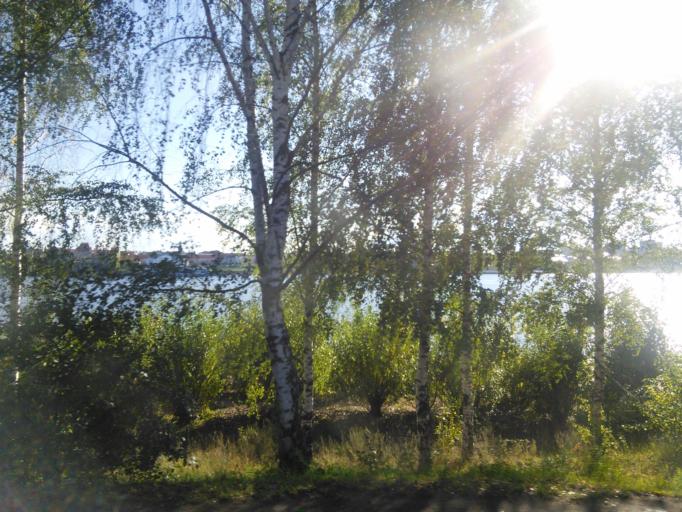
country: RU
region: Jaroslavl
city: Rybinsk
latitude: 58.0557
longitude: 38.8580
